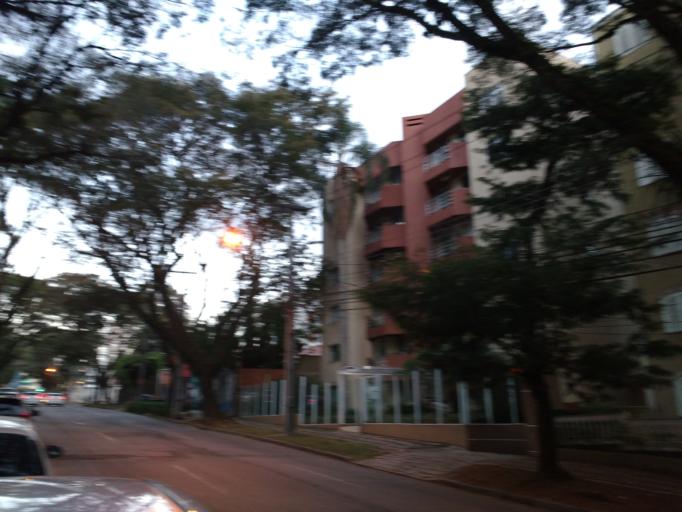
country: BR
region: Parana
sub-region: Curitiba
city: Curitiba
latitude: -25.4230
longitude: -49.2869
